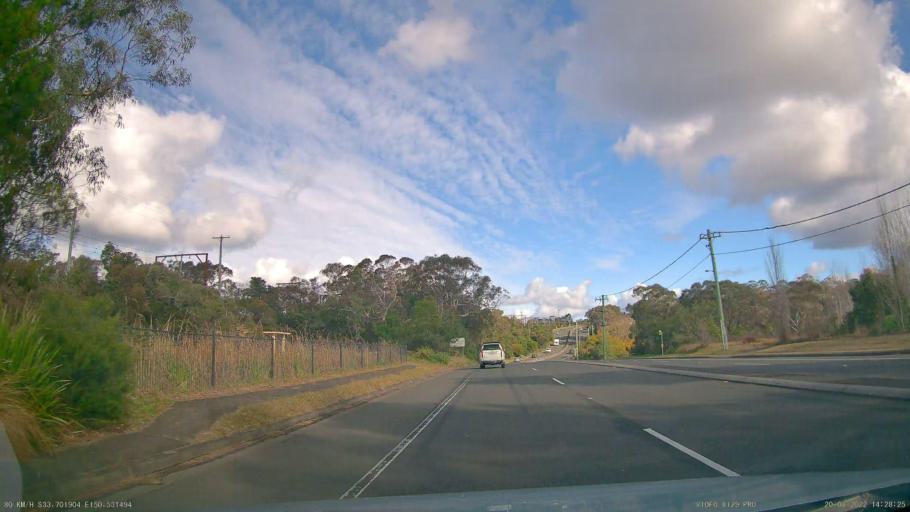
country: AU
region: New South Wales
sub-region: Blue Mountains Municipality
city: Hazelbrook
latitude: -33.7023
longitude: 150.5313
